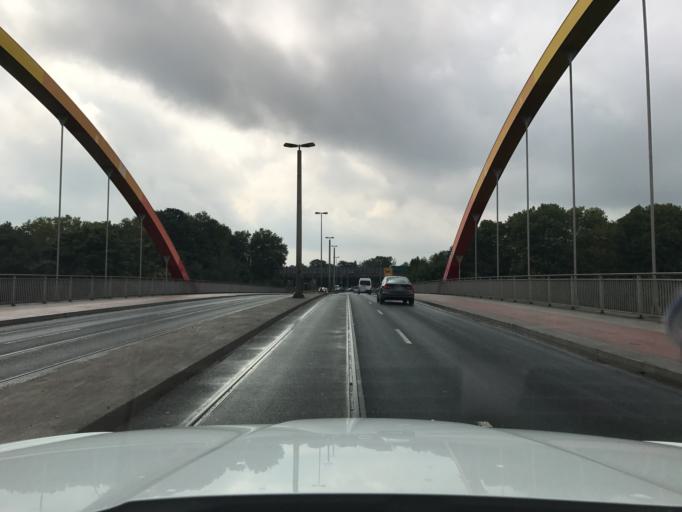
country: DE
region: North Rhine-Westphalia
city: Meiderich
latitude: 51.4502
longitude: 6.7919
